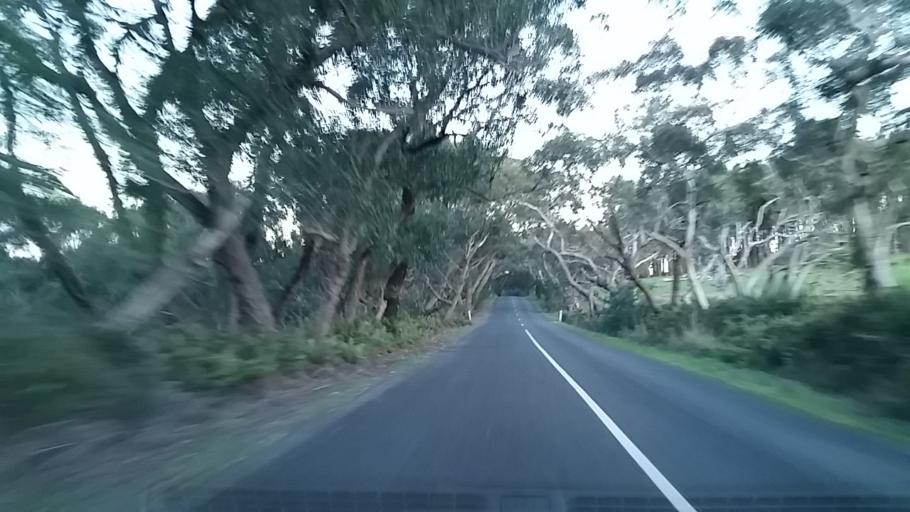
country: AU
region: South Australia
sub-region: Alexandrina
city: Mount Compass
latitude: -35.3076
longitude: 138.6148
